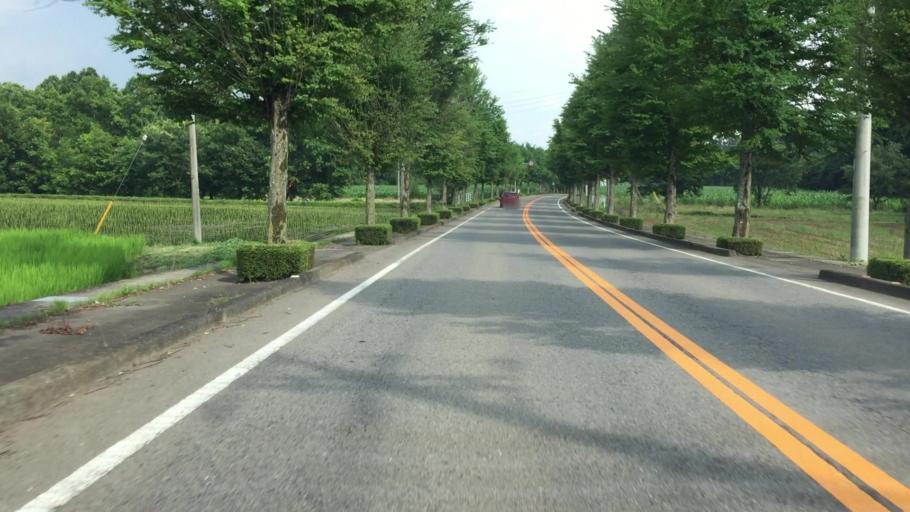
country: JP
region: Tochigi
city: Kuroiso
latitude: 36.9857
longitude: 139.9569
